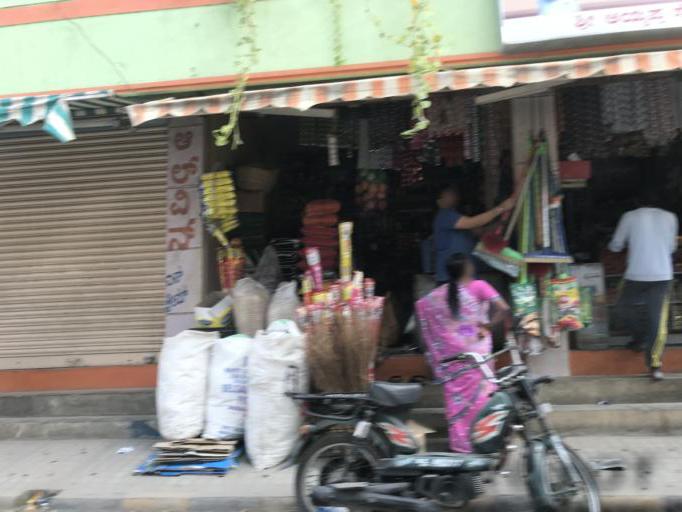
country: IN
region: Karnataka
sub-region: Bangalore Urban
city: Bangalore
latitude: 12.9996
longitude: 77.5274
